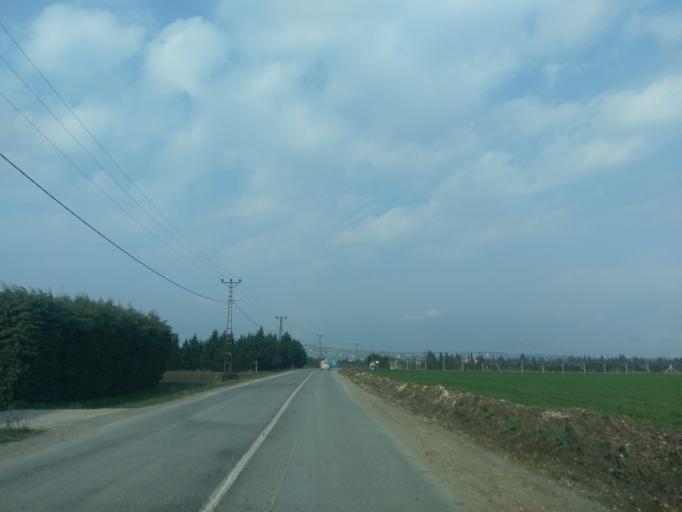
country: TR
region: Istanbul
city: Kavakli
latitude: 41.1103
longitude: 28.2987
